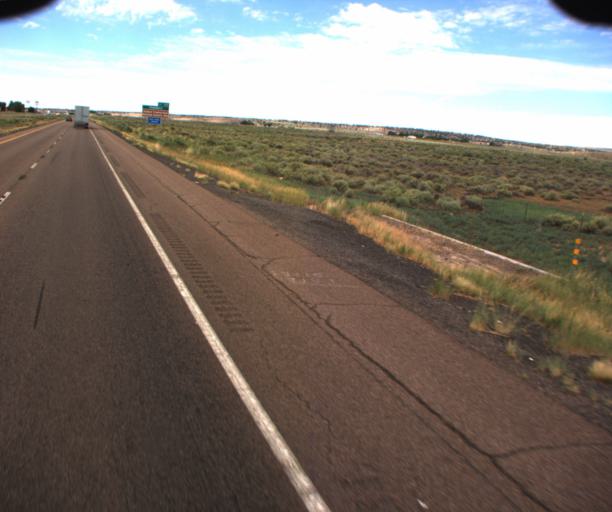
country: US
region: Arizona
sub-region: Apache County
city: Houck
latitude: 35.1937
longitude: -109.4215
